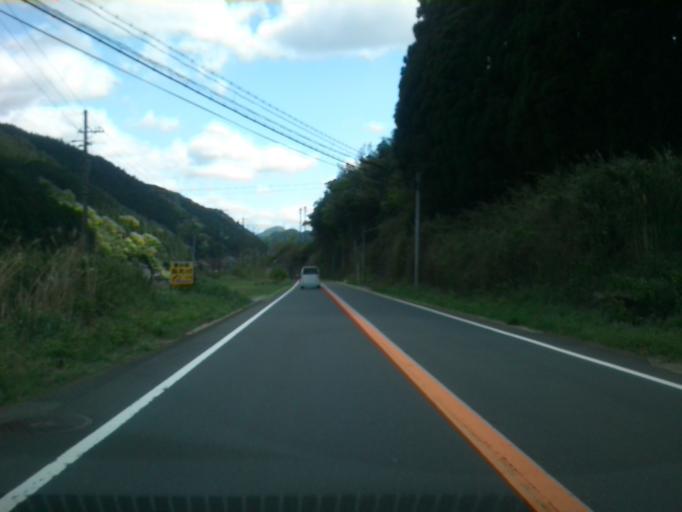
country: JP
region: Kyoto
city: Fukuchiyama
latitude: 35.3695
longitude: 135.0479
